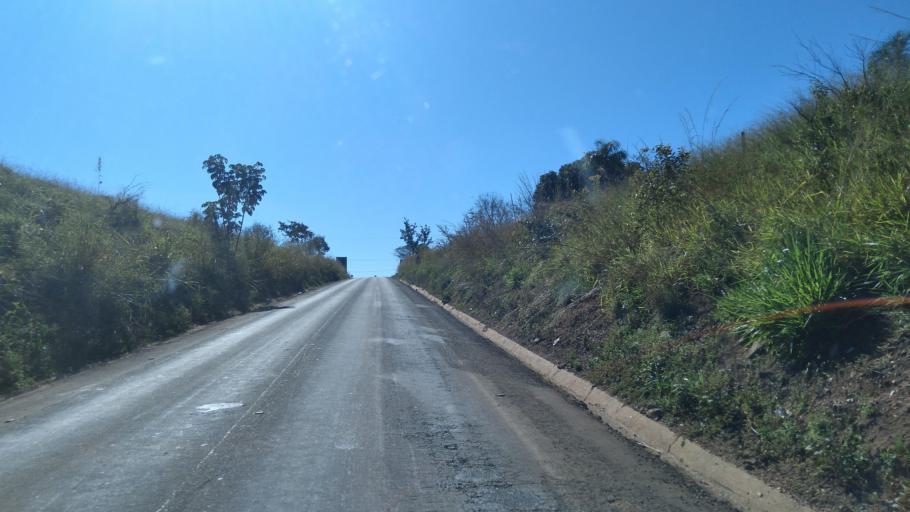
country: BR
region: Goias
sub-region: Mineiros
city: Mineiros
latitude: -17.5784
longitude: -52.5217
